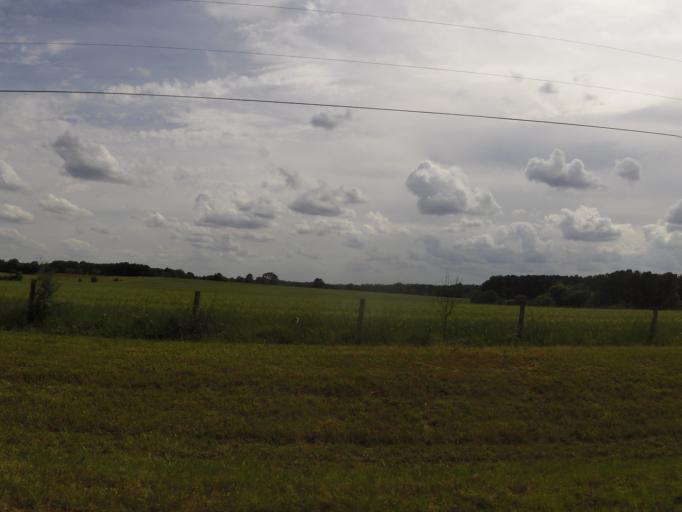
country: US
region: Georgia
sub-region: McDuffie County
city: Thomson
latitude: 33.5280
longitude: -82.4763
